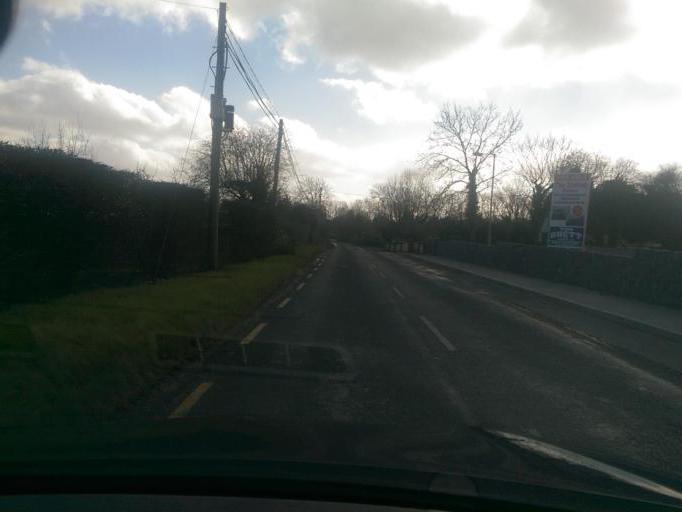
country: IE
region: Connaught
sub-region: County Galway
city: Athenry
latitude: 53.3711
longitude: -8.7014
